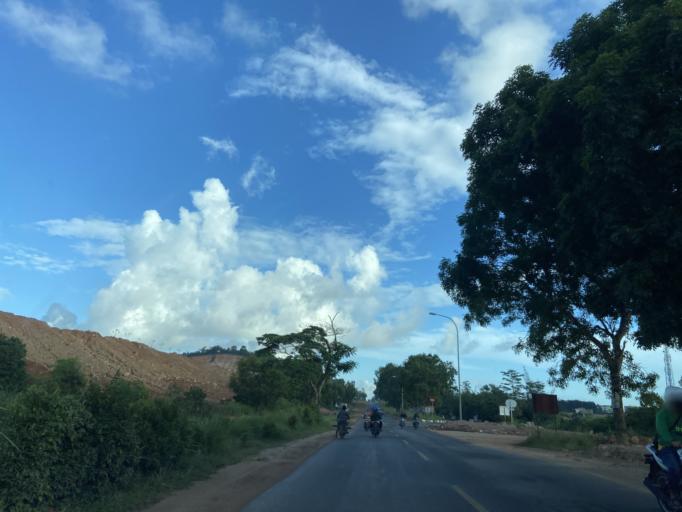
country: SG
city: Singapore
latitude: 1.0265
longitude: 104.0082
